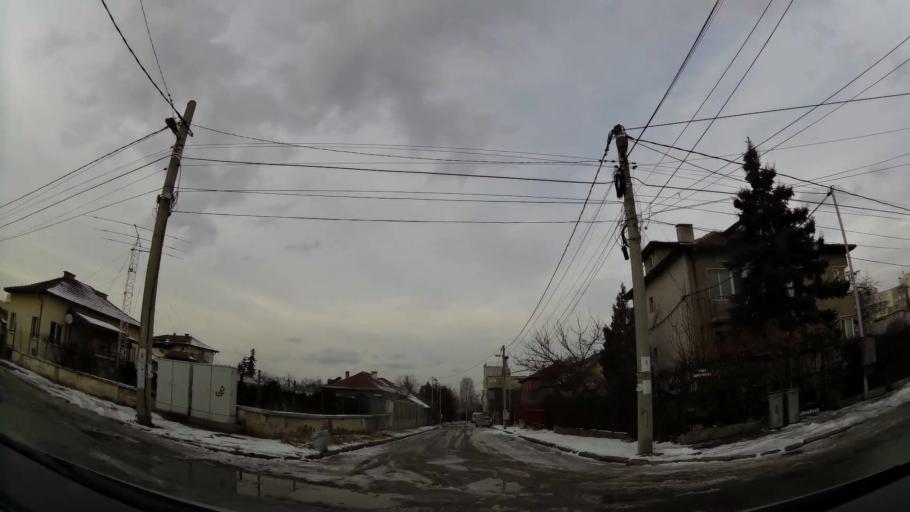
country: BG
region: Sofia-Capital
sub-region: Stolichna Obshtina
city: Sofia
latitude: 42.7269
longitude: 23.3436
